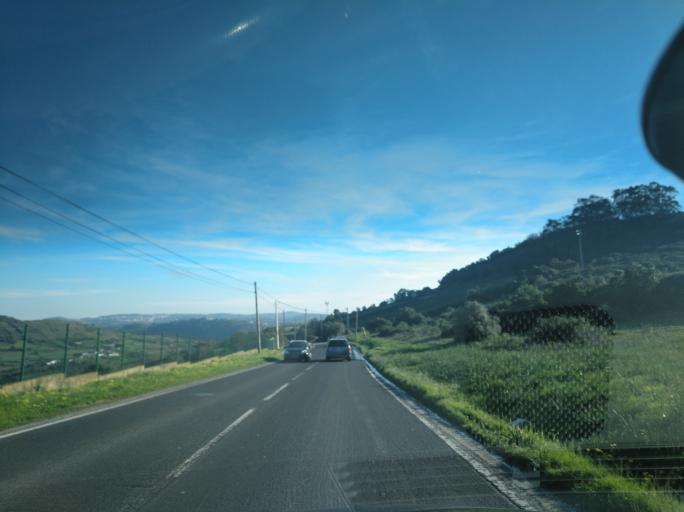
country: PT
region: Lisbon
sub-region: Mafra
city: Mafra
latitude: 38.9030
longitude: -9.3280
